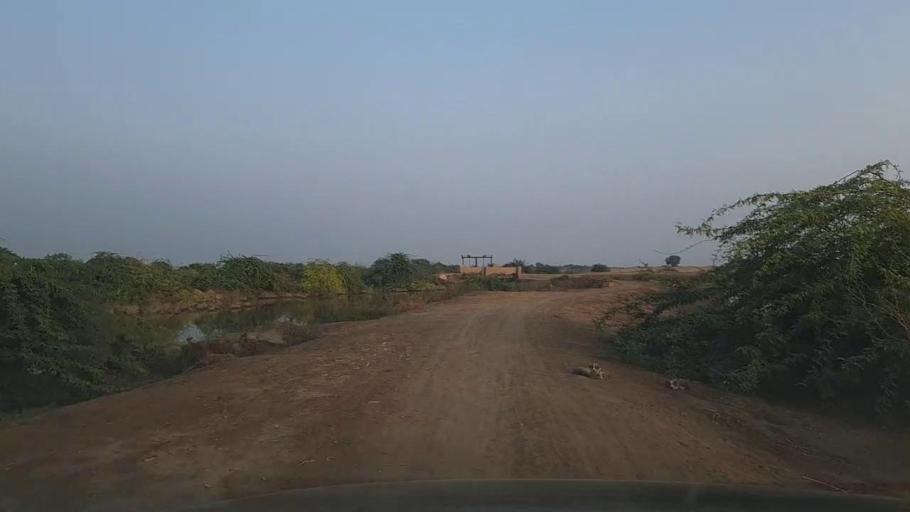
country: PK
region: Sindh
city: Jati
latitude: 24.5367
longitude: 68.4076
